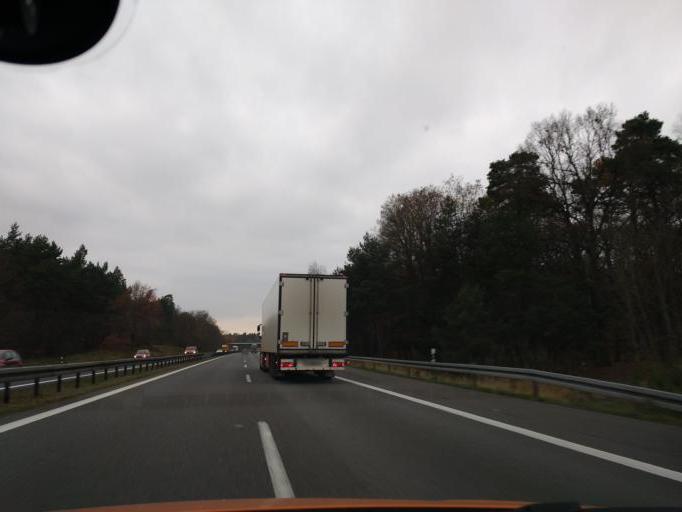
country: DE
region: Brandenburg
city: Fehrbellin
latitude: 52.7642
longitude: 12.8252
